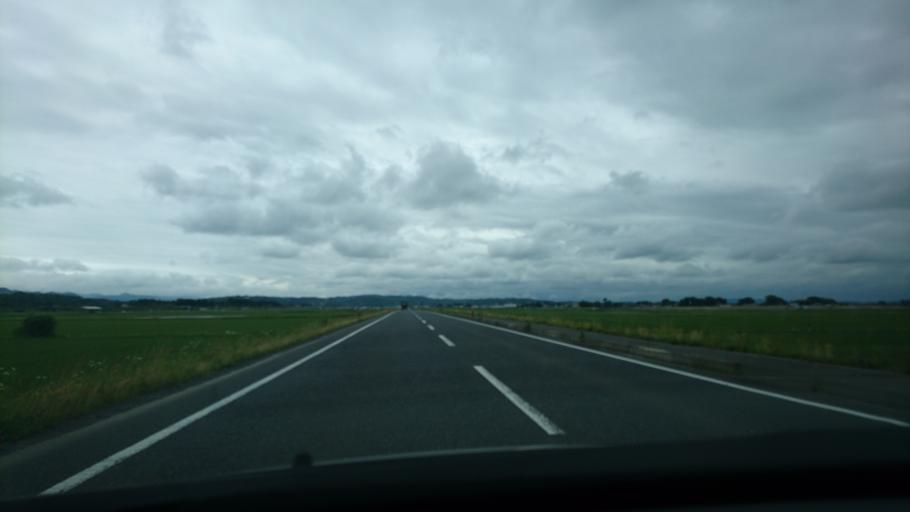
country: JP
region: Miyagi
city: Wakuya
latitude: 38.6859
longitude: 141.2609
